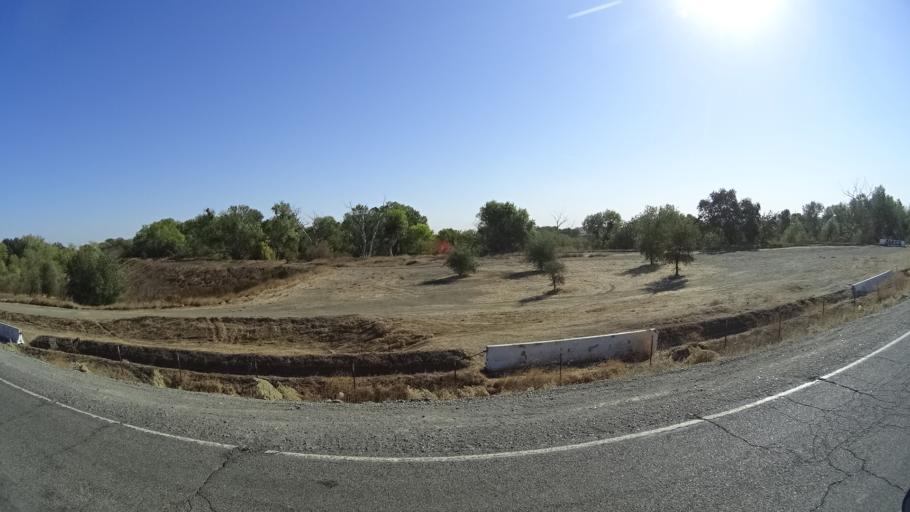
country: US
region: California
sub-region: Yolo County
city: Woodland
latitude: 38.6899
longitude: -121.8657
